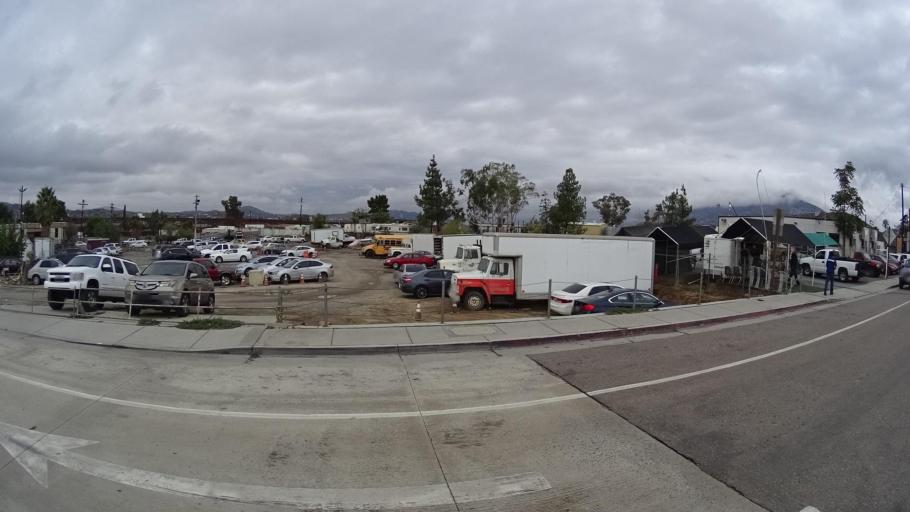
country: MX
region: Baja California
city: Tecate
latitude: 32.5783
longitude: -116.6284
